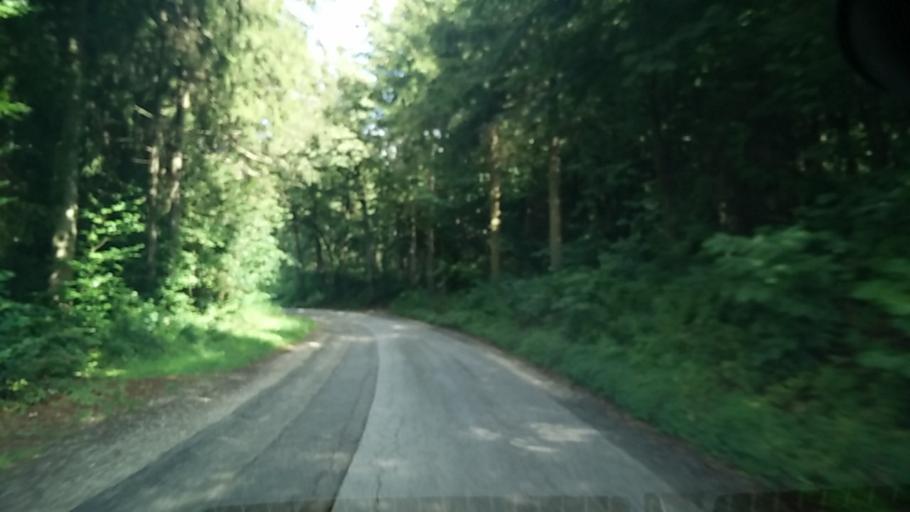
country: AT
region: Carinthia
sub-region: Politischer Bezirk Sankt Veit an der Glan
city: Bruckl
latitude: 46.7185
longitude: 14.5404
